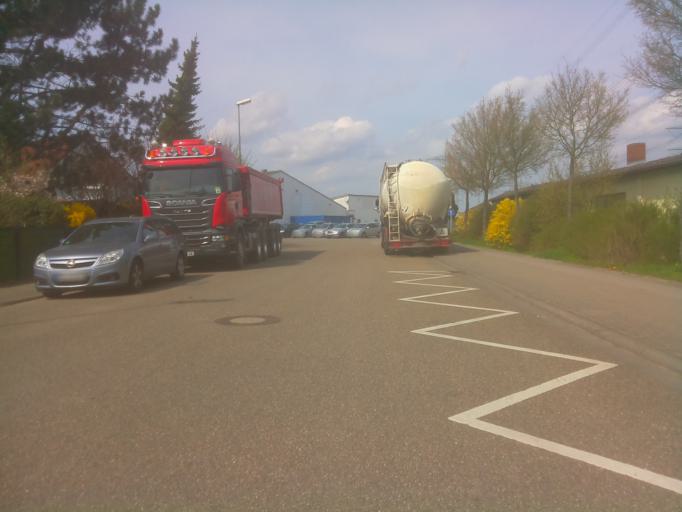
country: DE
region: Hesse
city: Lampertheim
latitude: 49.5994
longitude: 8.4863
